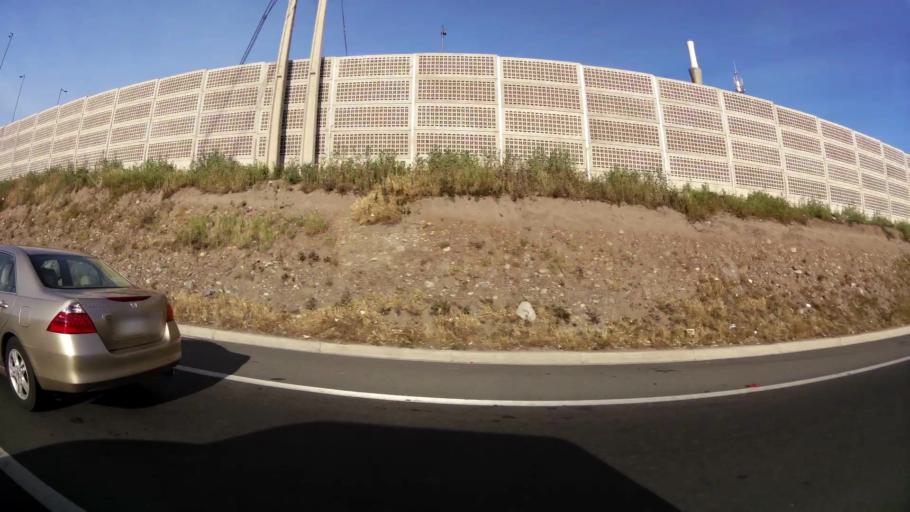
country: CL
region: Santiago Metropolitan
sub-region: Provincia de Santiago
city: La Pintana
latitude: -33.5829
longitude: -70.6109
